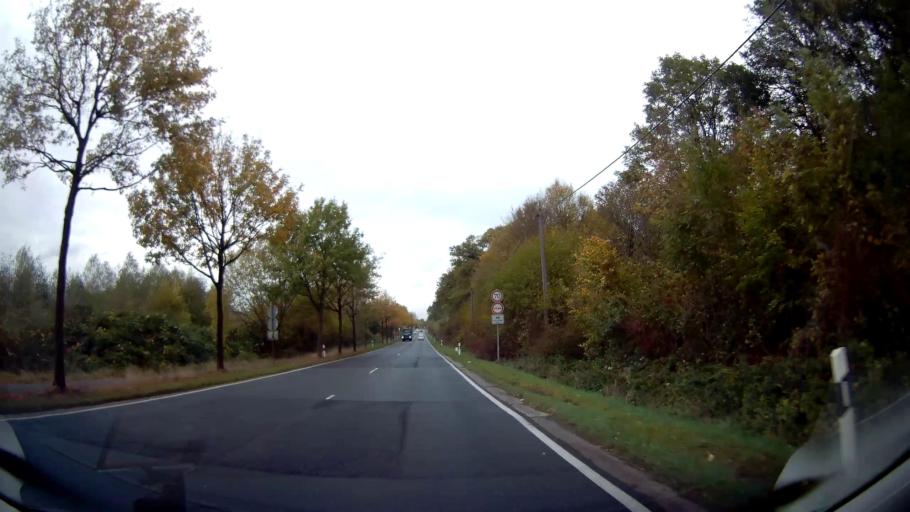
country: DE
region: North Rhine-Westphalia
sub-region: Regierungsbezirk Munster
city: Bottrop
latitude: 51.5845
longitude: 6.9135
